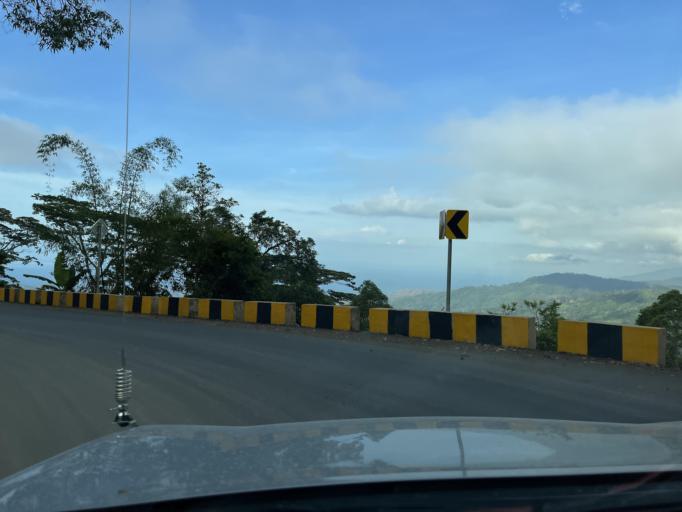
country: TL
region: Dili
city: Dili
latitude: -8.6185
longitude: 125.6389
